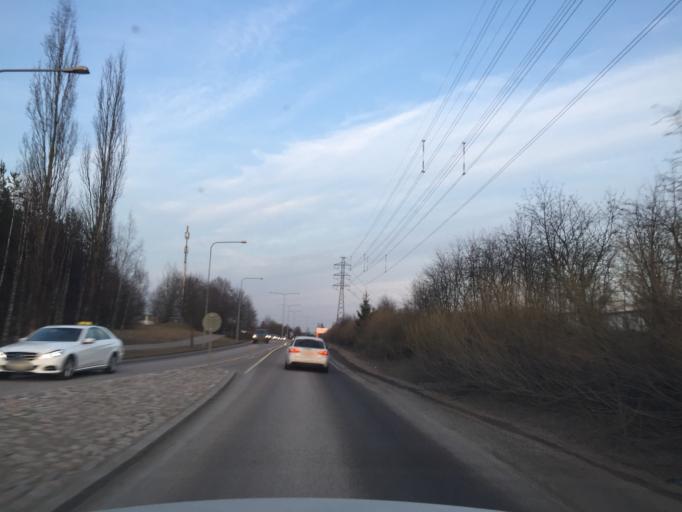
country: FI
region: Uusimaa
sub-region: Helsinki
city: Vantaa
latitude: 60.2644
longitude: 24.9847
